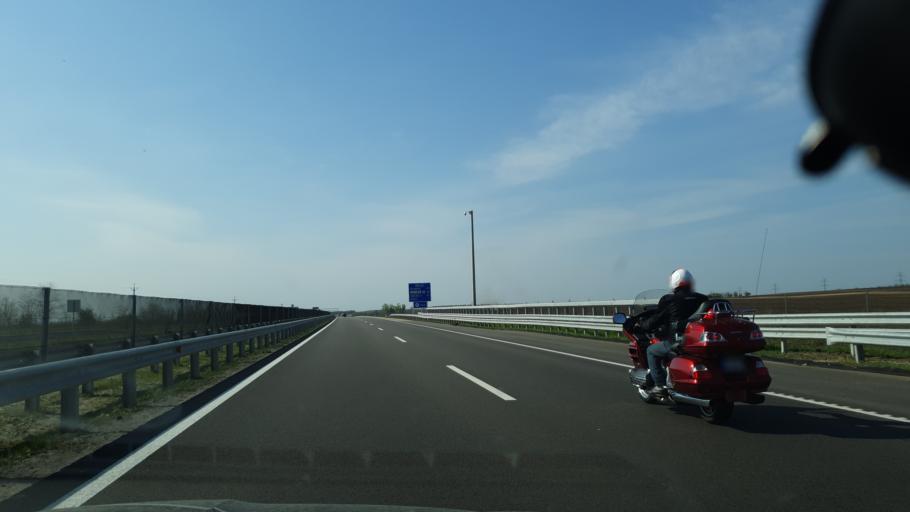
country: HU
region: Pest
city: Pilis
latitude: 47.3148
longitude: 19.5499
